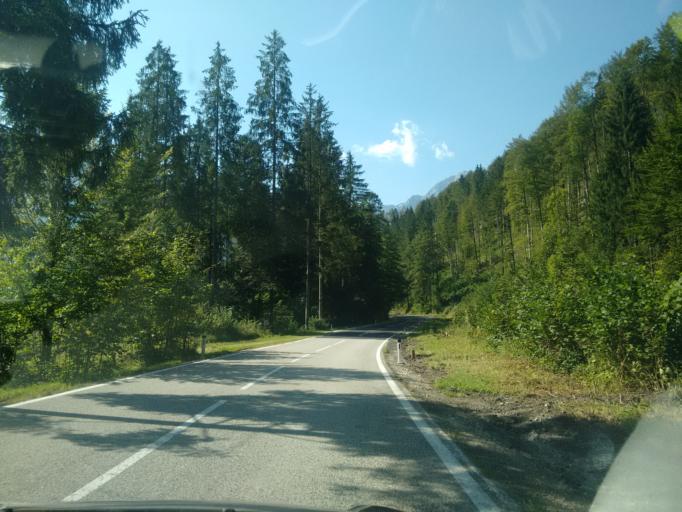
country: AT
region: Upper Austria
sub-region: Politischer Bezirk Gmunden
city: Gruenau im Almtal
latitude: 47.7575
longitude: 13.9537
